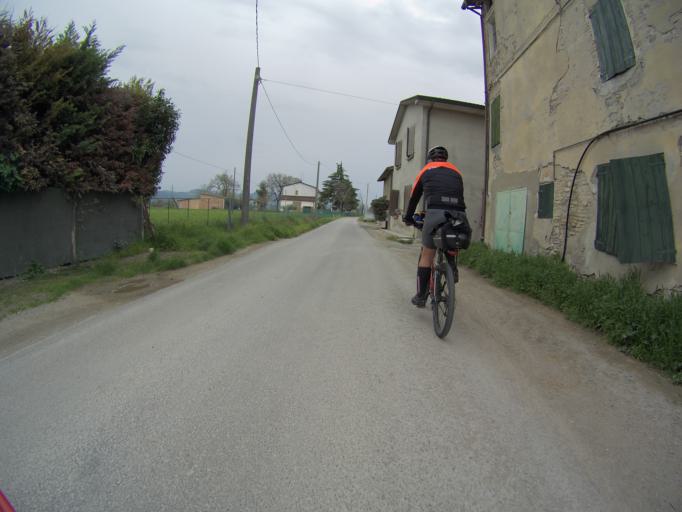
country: IT
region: Emilia-Romagna
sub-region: Provincia di Parma
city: Montechiarugolo
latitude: 44.6610
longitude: 10.4365
